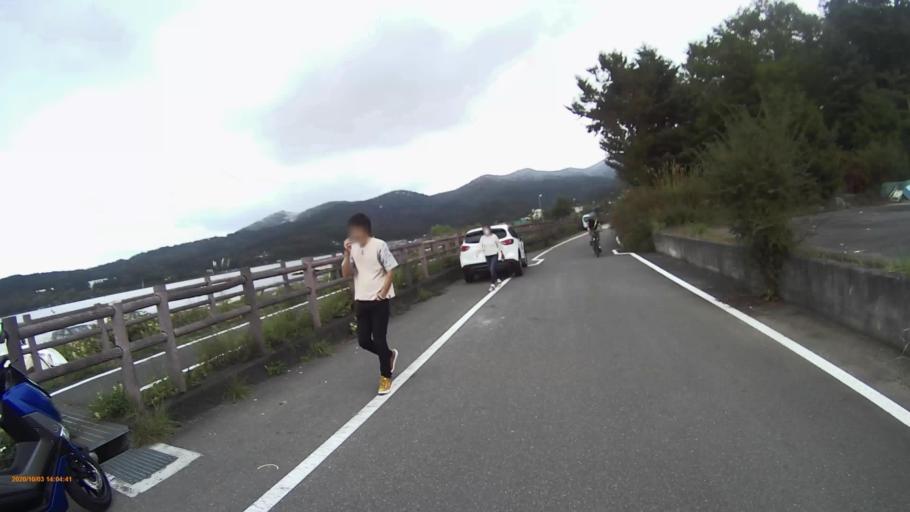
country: JP
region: Shizuoka
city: Gotemba
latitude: 35.4222
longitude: 138.9018
